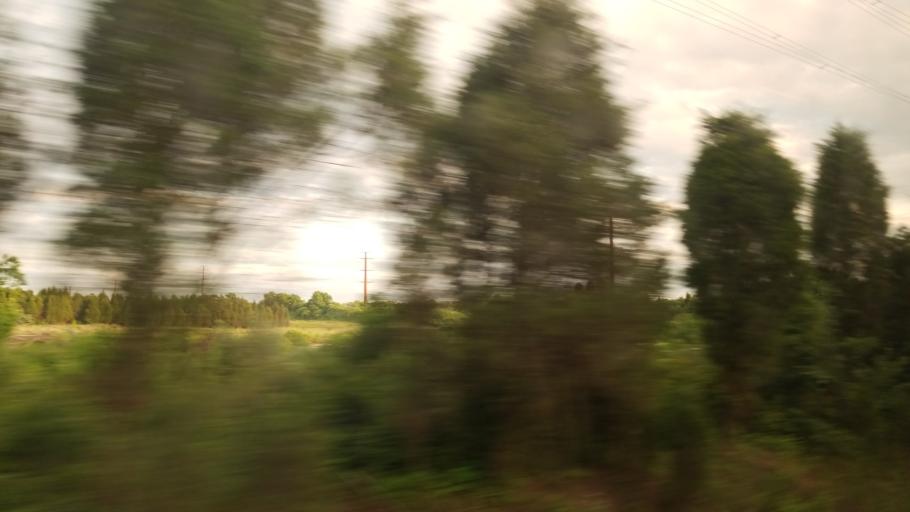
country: US
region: Virginia
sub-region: City of Manassas
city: Manassas
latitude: 38.7383
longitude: -77.5110
